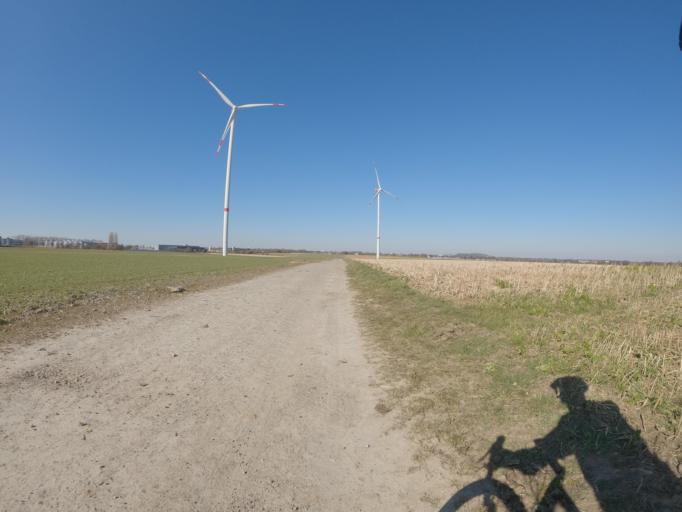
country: NL
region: Limburg
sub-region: Gemeente Simpelveld
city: Simpelveld
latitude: 50.8357
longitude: 6.0274
